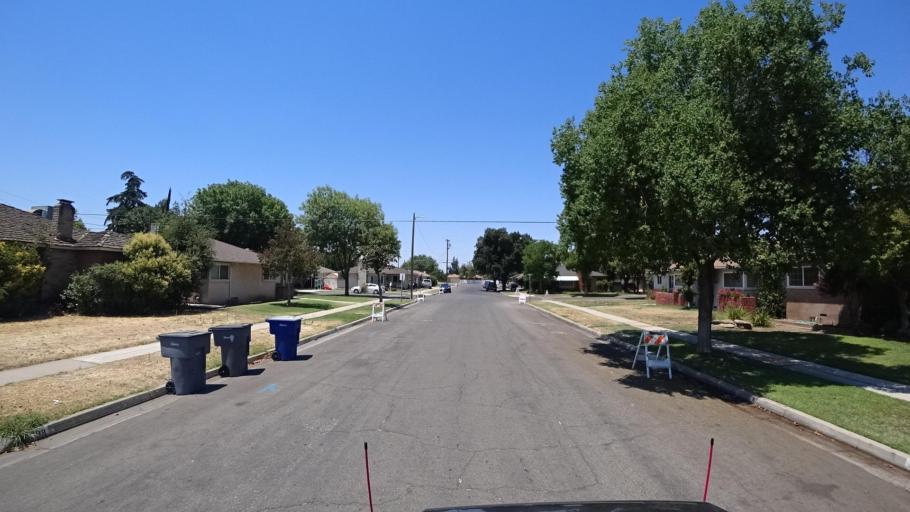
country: US
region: California
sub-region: Fresno County
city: Fresno
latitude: 36.7958
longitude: -119.7706
